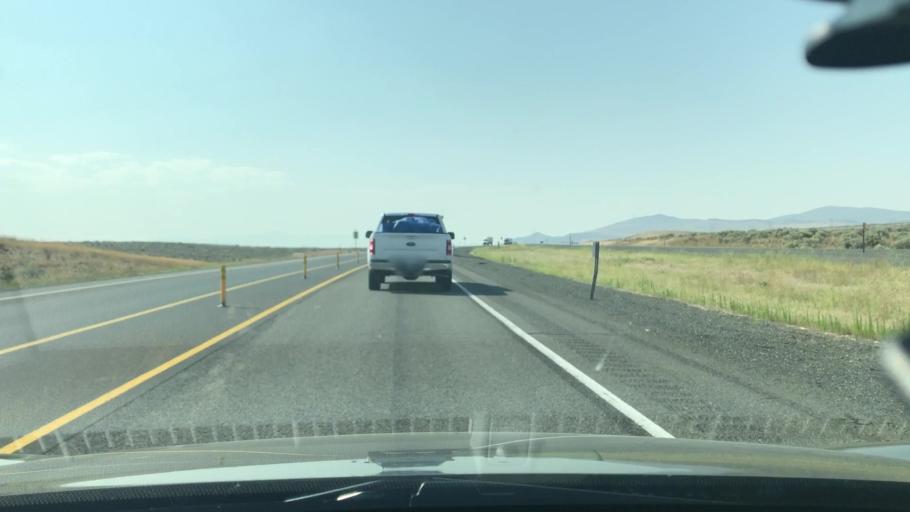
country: US
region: Oregon
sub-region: Baker County
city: Baker City
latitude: 44.6891
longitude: -117.6823
